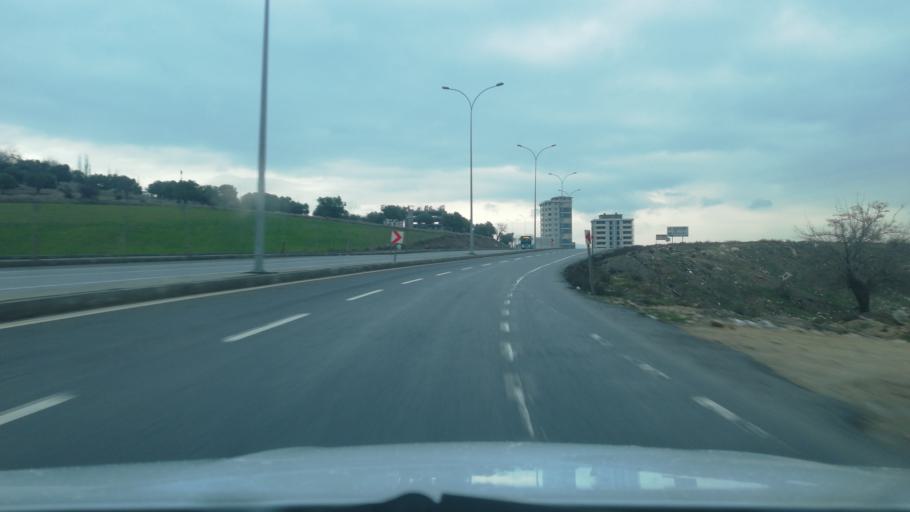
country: TR
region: Kahramanmaras
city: Kahramanmaras
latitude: 37.5816
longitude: 36.9910
